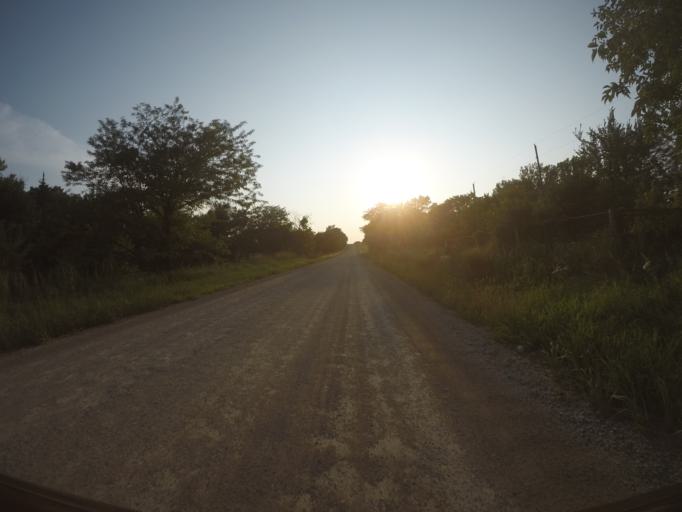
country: US
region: Kansas
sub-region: Riley County
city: Manhattan
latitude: 39.1304
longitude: -96.4448
